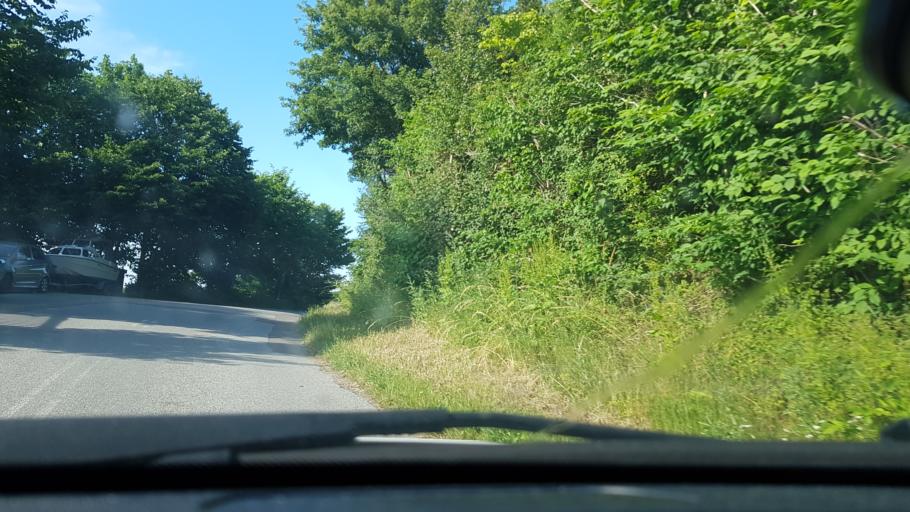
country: DK
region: Zealand
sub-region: Odsherred Kommune
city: Hojby
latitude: 55.8870
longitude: 11.6084
